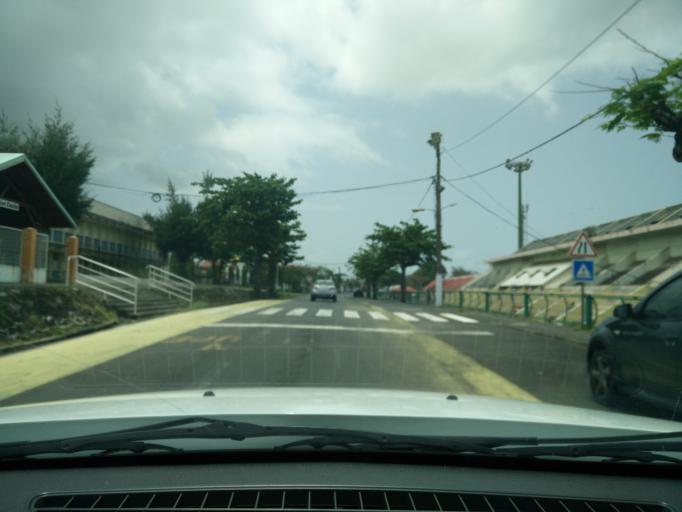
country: GP
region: Guadeloupe
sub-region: Guadeloupe
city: Capesterre-Belle-Eau
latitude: 16.0481
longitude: -61.5629
